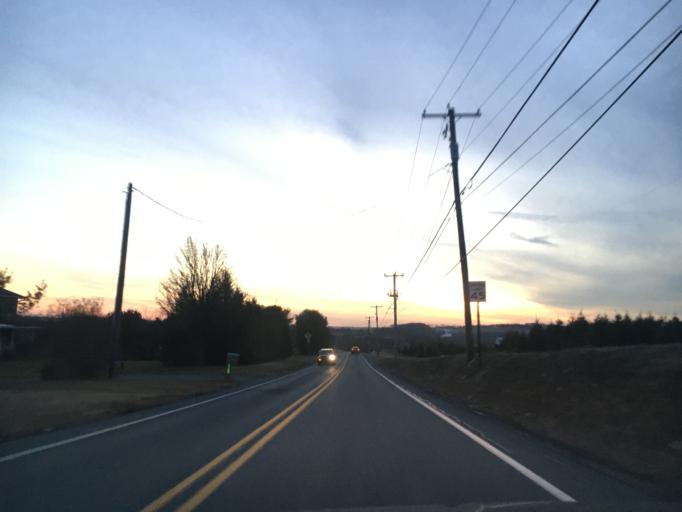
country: US
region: Pennsylvania
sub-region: Northampton County
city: Youngsville
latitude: 40.7584
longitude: -75.4649
